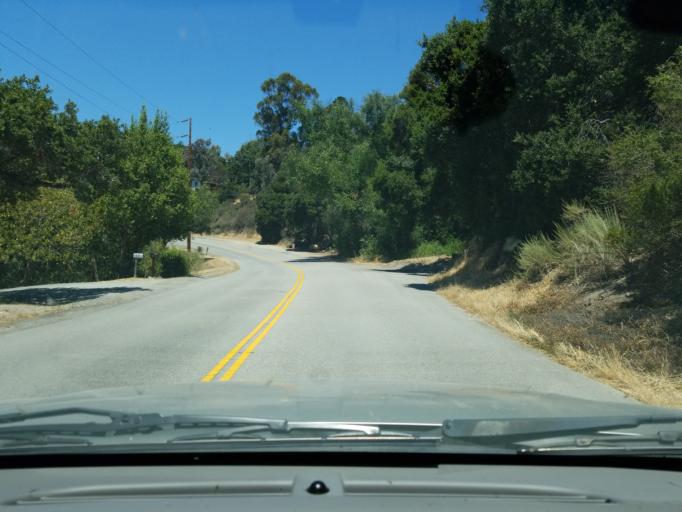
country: US
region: California
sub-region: Monterey County
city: Carmel Valley Village
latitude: 36.4752
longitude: -121.7187
